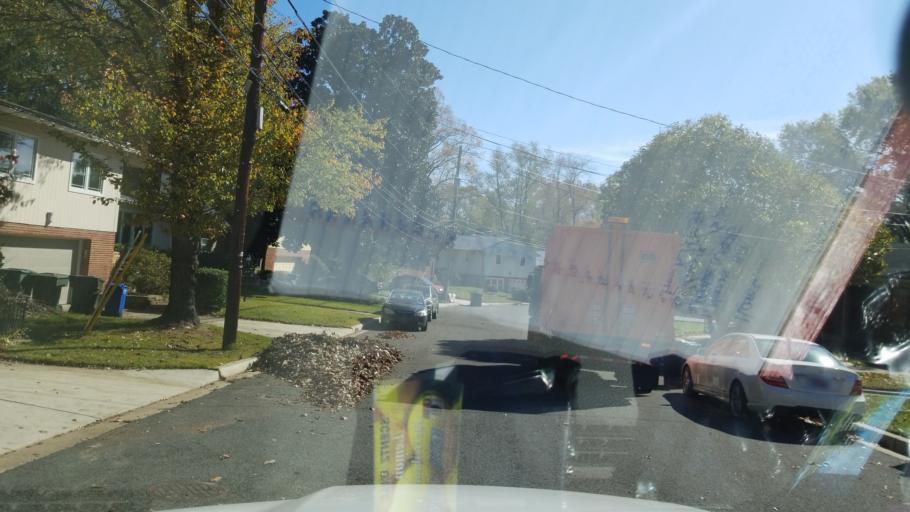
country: US
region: Maryland
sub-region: Montgomery County
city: Silver Spring
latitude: 38.9931
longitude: -77.0381
